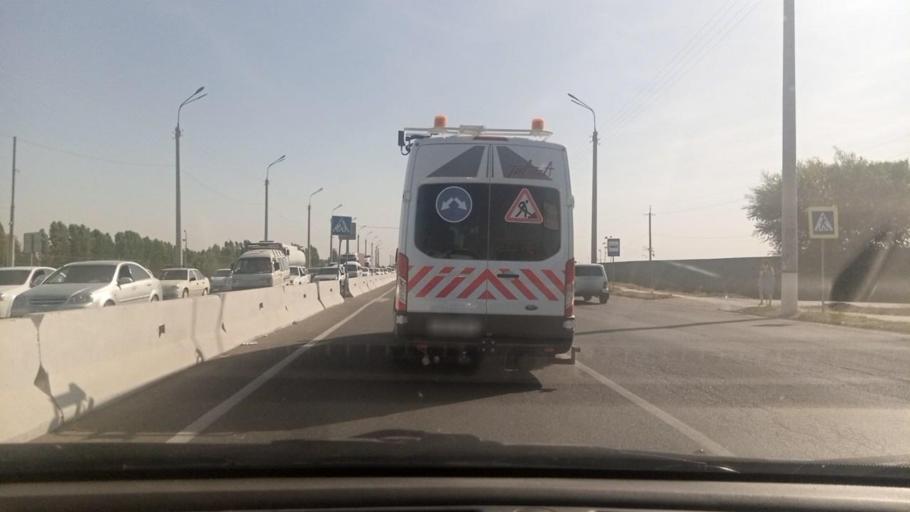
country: UZ
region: Toshkent Shahri
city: Bektemir
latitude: 41.2023
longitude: 69.3328
